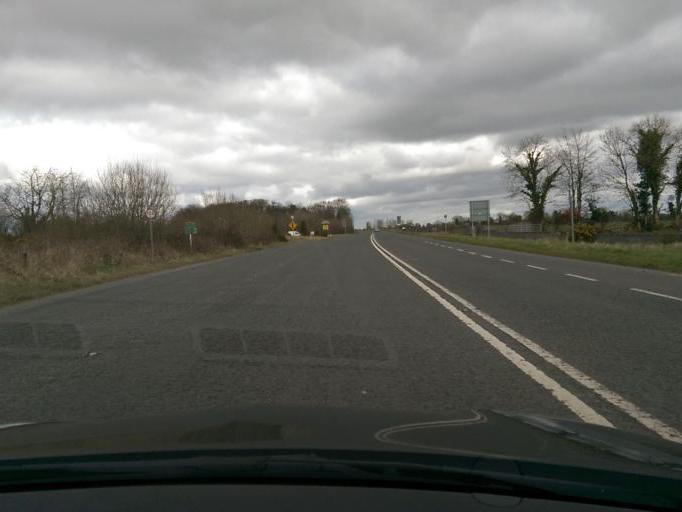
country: IE
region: Leinster
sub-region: An Iarmhi
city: Athlone
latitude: 53.3622
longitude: -8.0668
